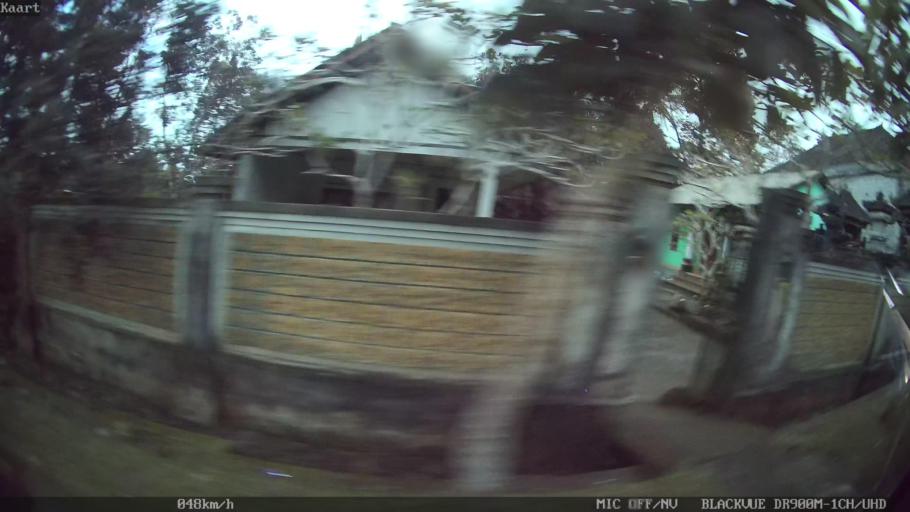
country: ID
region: Bali
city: Banjar Geriana Kangin
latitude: -8.3877
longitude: 115.4450
